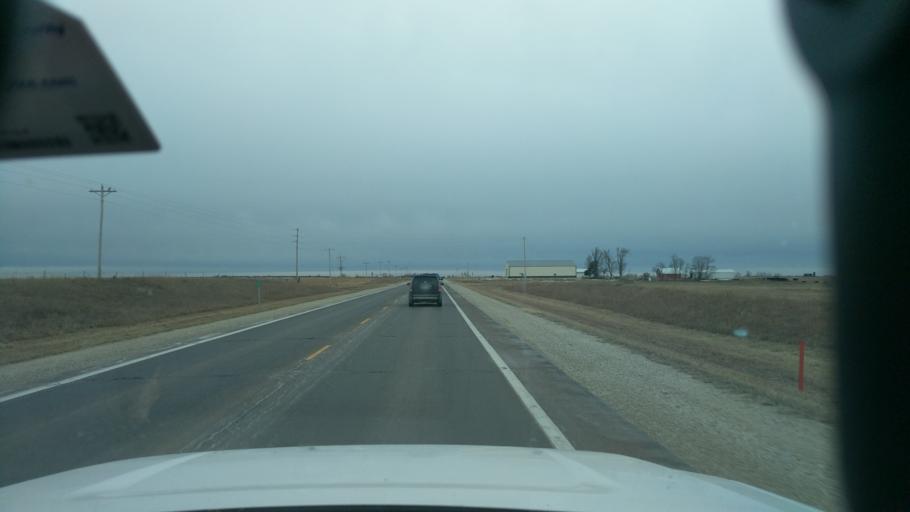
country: US
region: Kansas
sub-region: Dickinson County
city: Herington
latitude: 38.6253
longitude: -96.9488
